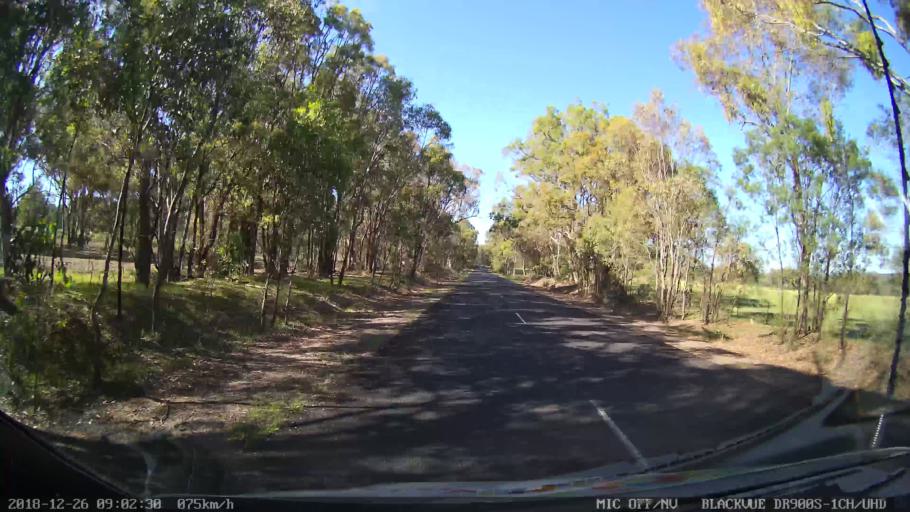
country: AU
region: New South Wales
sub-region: Mid-Western Regional
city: Kandos
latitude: -32.6534
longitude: 150.0188
